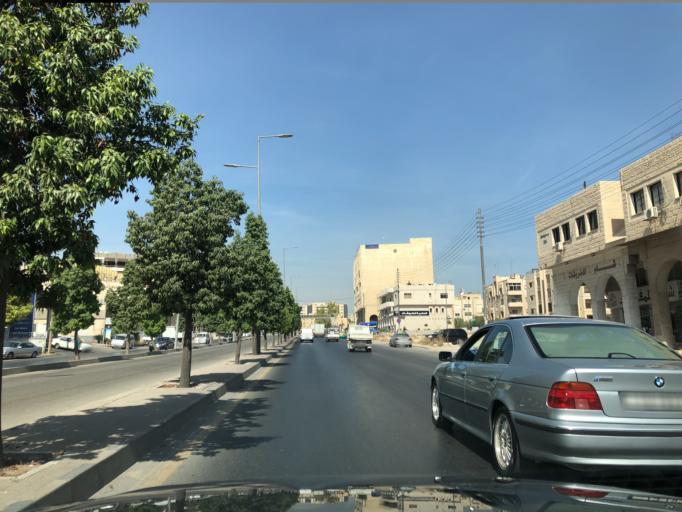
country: JO
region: Amman
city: Al Jubayhah
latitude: 32.0212
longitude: 35.8621
